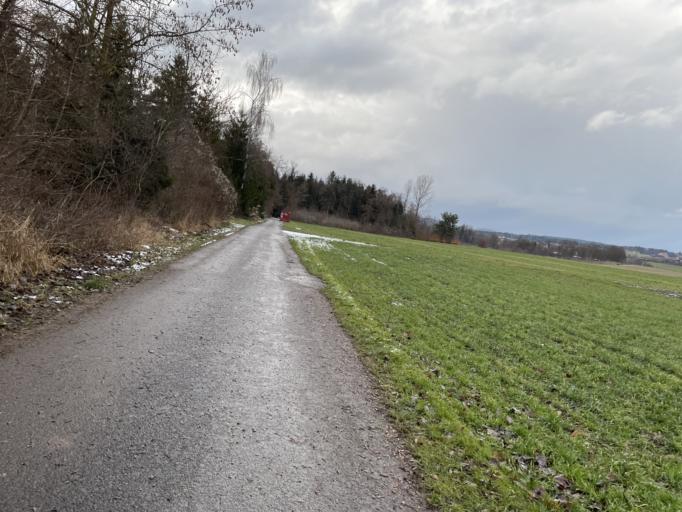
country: CH
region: Bern
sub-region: Bern-Mittelland District
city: Munsingen
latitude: 46.8816
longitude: 7.5468
